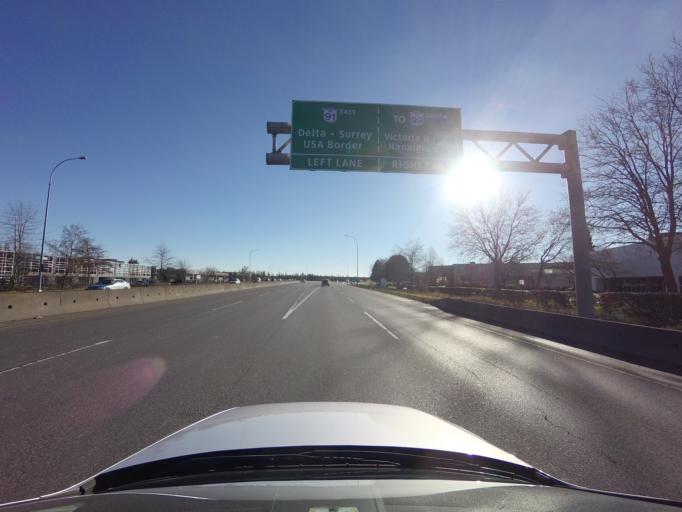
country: CA
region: British Columbia
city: Richmond
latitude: 49.1816
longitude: -123.0760
